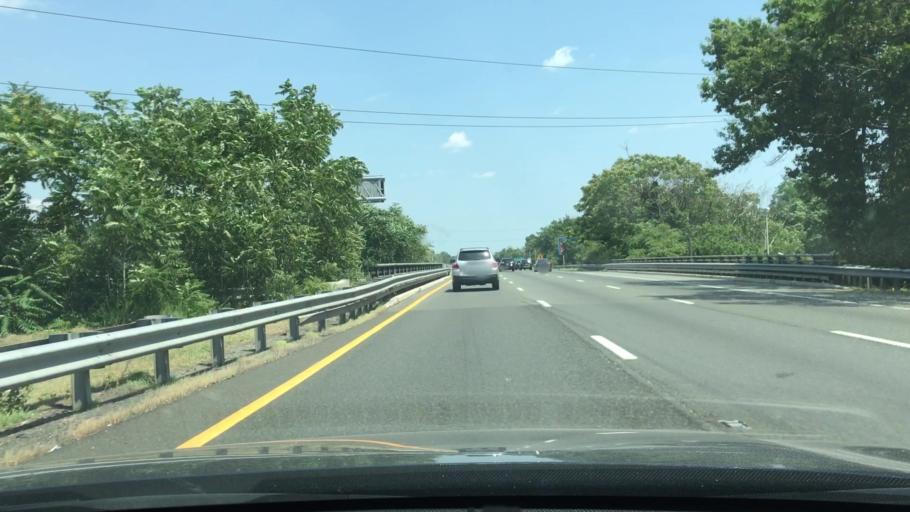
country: US
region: New Jersey
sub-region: Middlesex County
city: Society Hill
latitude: 40.5565
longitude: -74.4626
